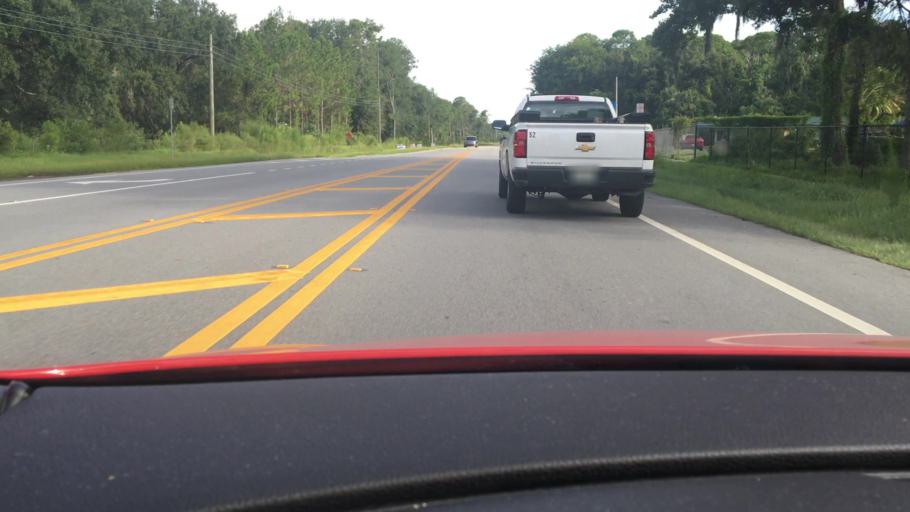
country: US
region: Florida
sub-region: Volusia County
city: Daytona Beach
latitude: 29.1688
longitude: -81.0878
